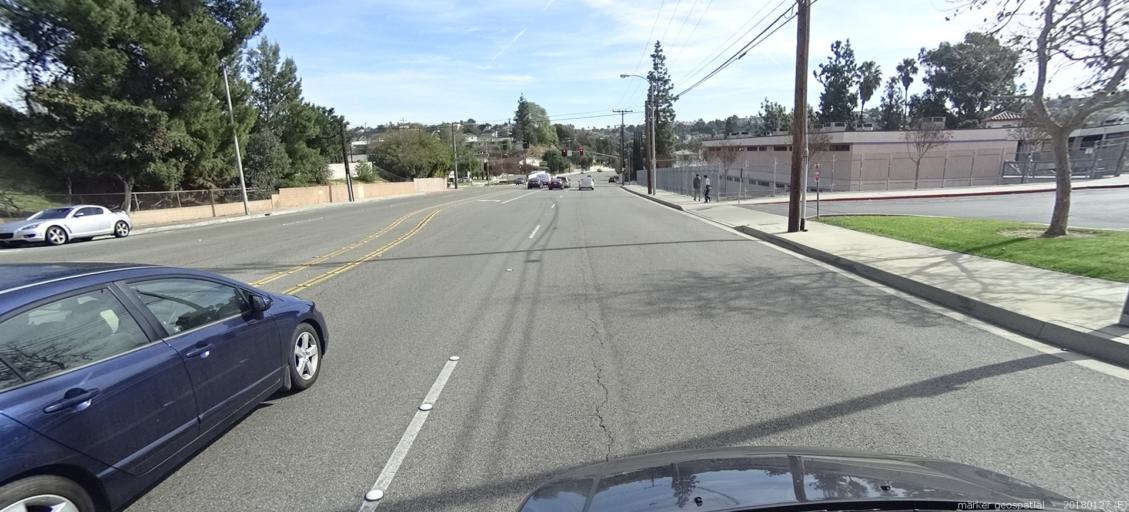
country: US
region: California
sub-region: Los Angeles County
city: Walnut
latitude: 33.9839
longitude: -117.8380
